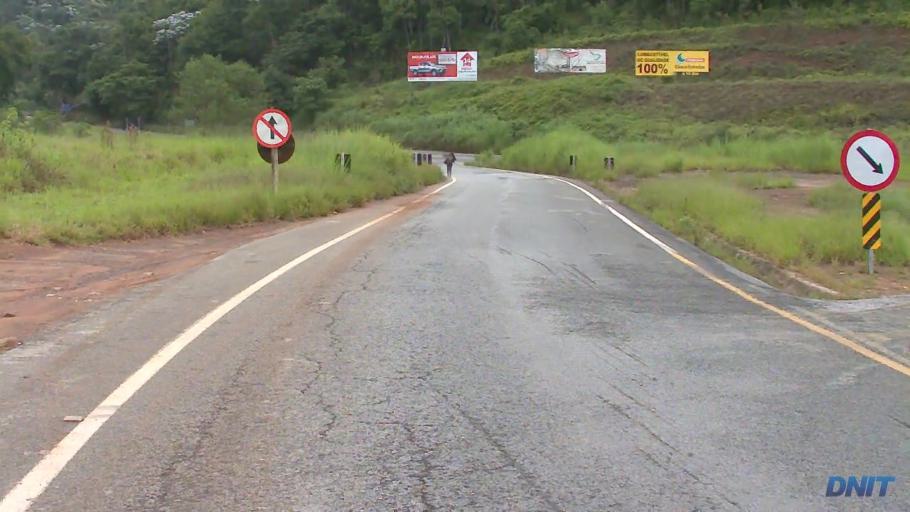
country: BR
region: Minas Gerais
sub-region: Joao Monlevade
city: Joao Monlevade
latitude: -19.8614
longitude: -43.1168
